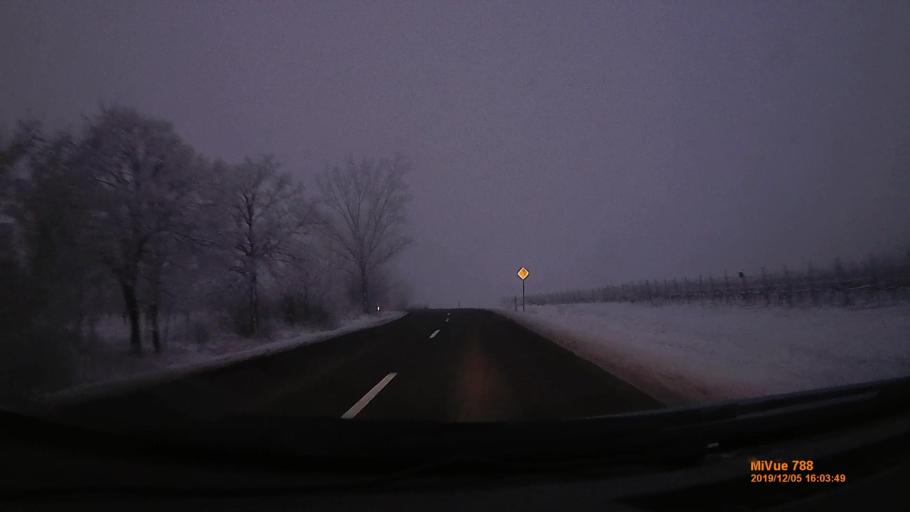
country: HU
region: Borsod-Abauj-Zemplen
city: Tarcal
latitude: 48.1050
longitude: 21.3625
